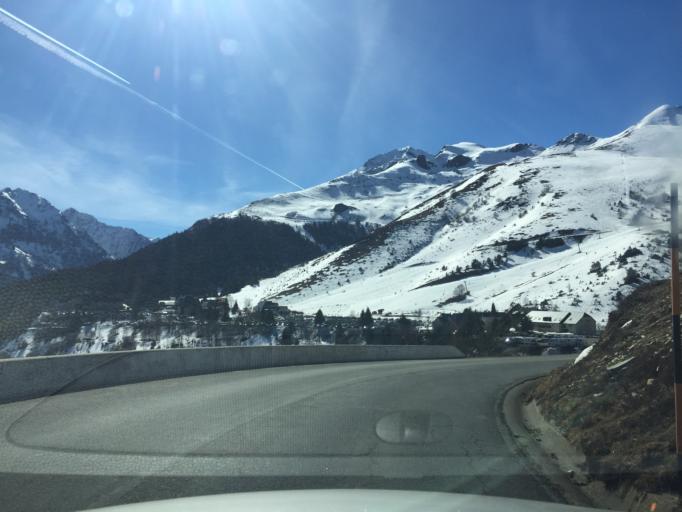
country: FR
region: Midi-Pyrenees
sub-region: Departement des Hautes-Pyrenees
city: Saint-Lary-Soulan
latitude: 42.7959
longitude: 0.3879
